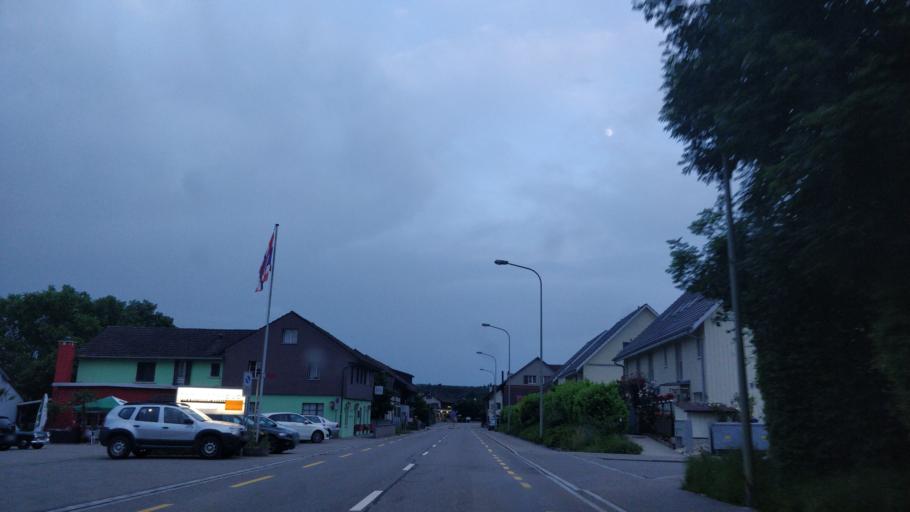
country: CH
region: Zurich
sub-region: Bezirk Buelach
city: Rorbas
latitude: 47.5332
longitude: 8.5716
